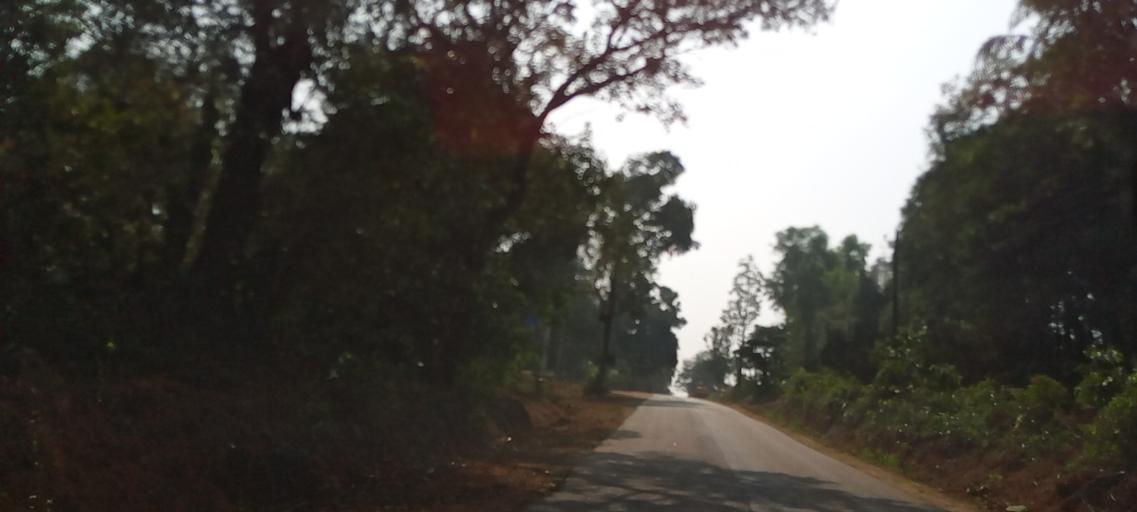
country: IN
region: Karnataka
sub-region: Udupi
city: Someshwar
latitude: 13.5321
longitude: 74.9177
